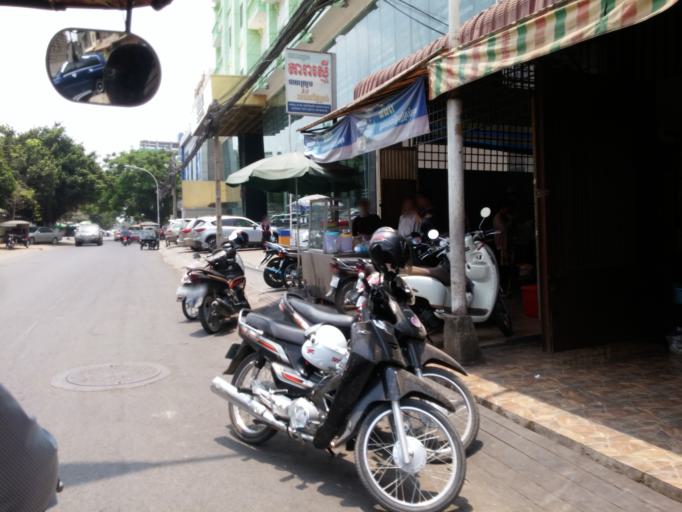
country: KH
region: Phnom Penh
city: Phnom Penh
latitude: 11.5569
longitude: 104.9192
